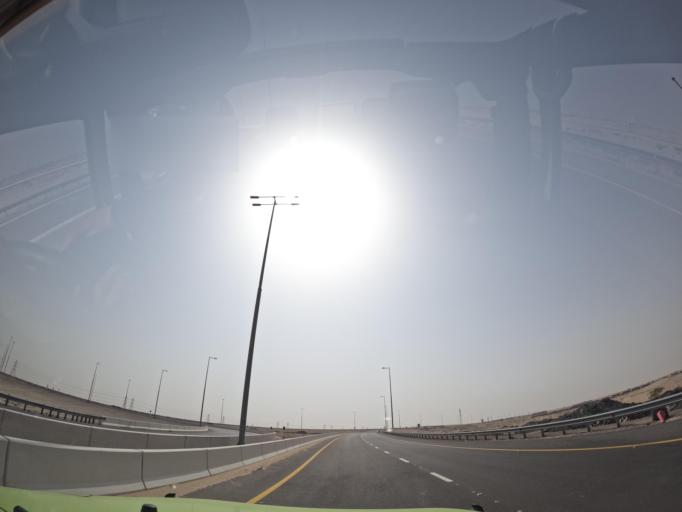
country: AE
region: Dubai
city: Dubai
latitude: 24.7888
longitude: 55.0767
